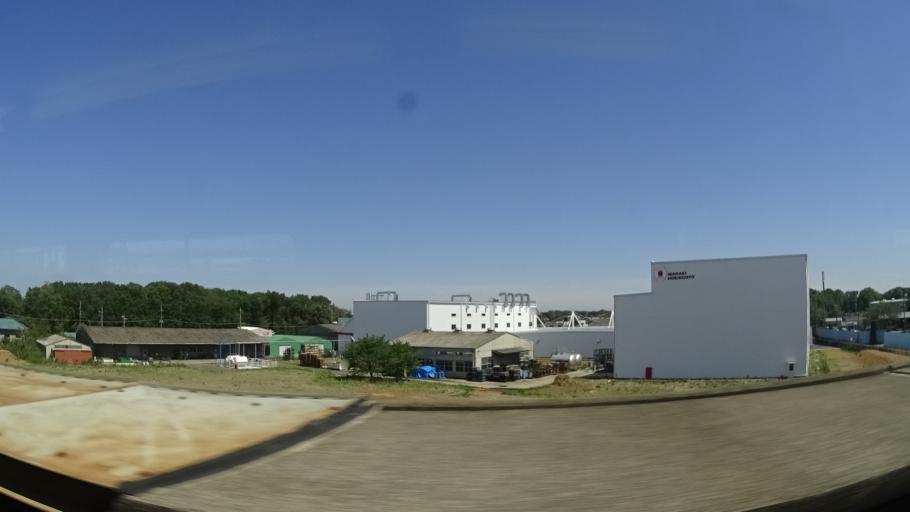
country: JP
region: Ibaraki
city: Koga
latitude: 36.1582
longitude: 139.7299
